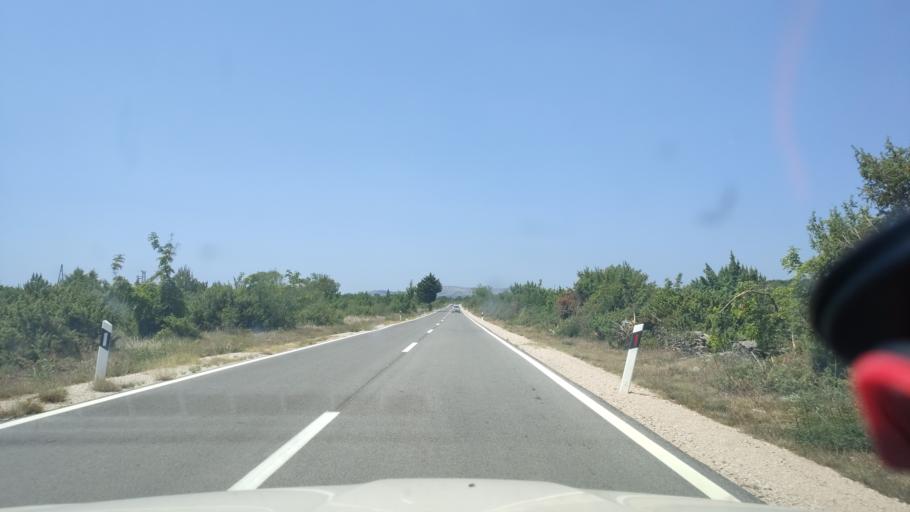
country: HR
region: Sibensko-Kniniska
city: Kistanje
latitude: 43.9713
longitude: 15.8893
